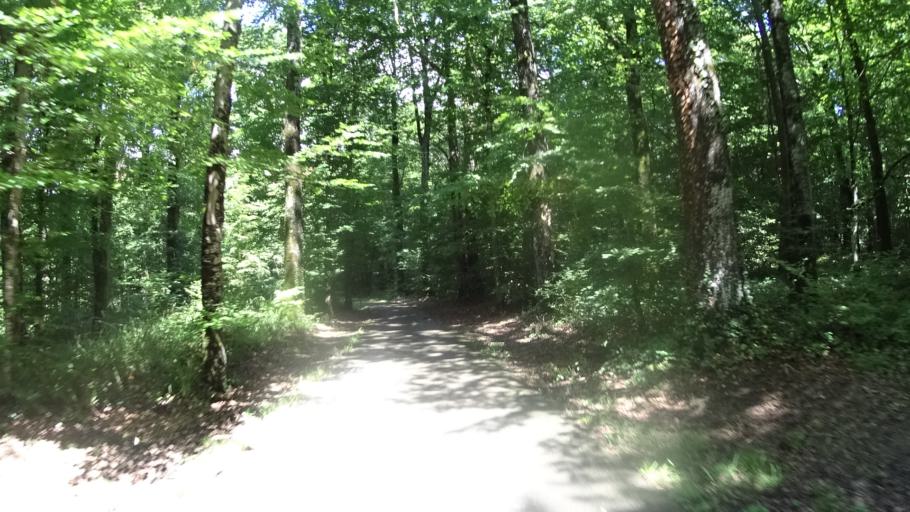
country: FR
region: Champagne-Ardenne
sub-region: Departement de la Haute-Marne
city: Montier-en-Der
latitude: 48.5331
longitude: 4.7724
